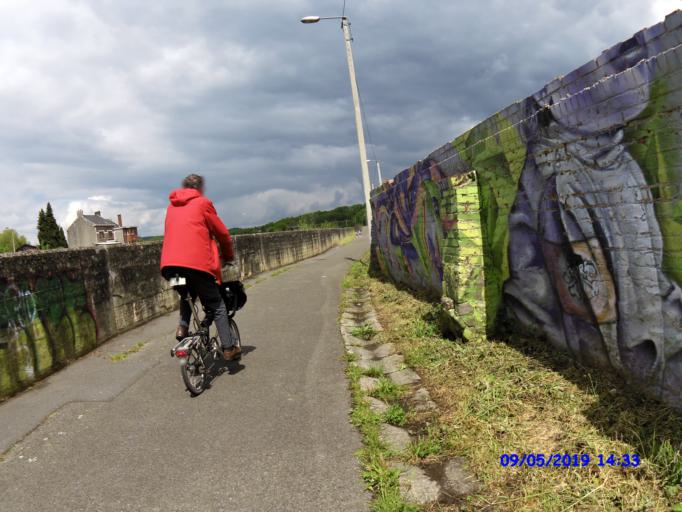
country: BE
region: Wallonia
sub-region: Province du Hainaut
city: Aiseau
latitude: 50.4318
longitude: 4.6170
